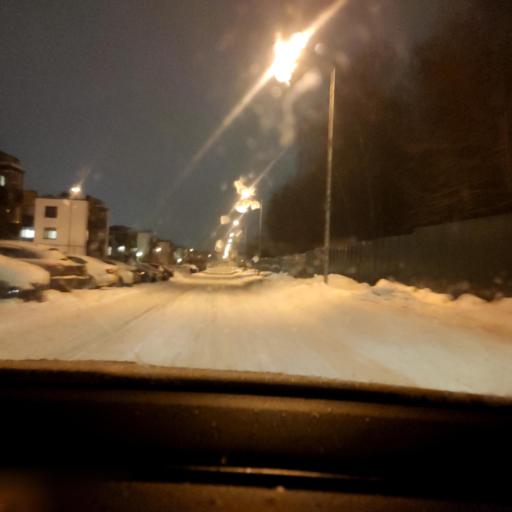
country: RU
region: Moskovskaya
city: Rozhdestveno
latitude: 55.8034
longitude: 36.9891
